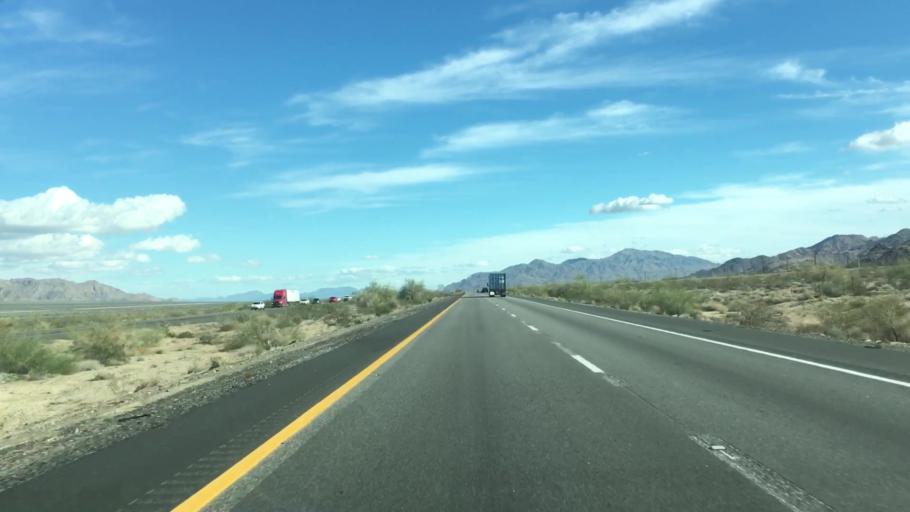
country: US
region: California
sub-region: Riverside County
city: Mecca
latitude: 33.6689
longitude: -115.6439
